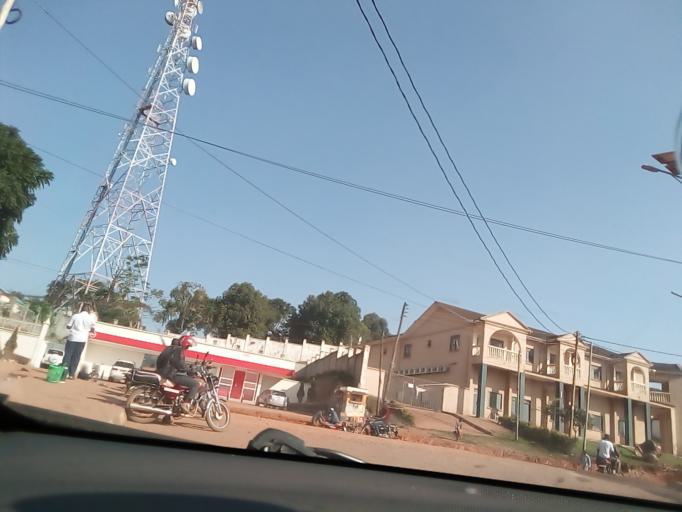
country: UG
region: Central Region
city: Masaka
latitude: -0.3430
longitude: 31.7370
